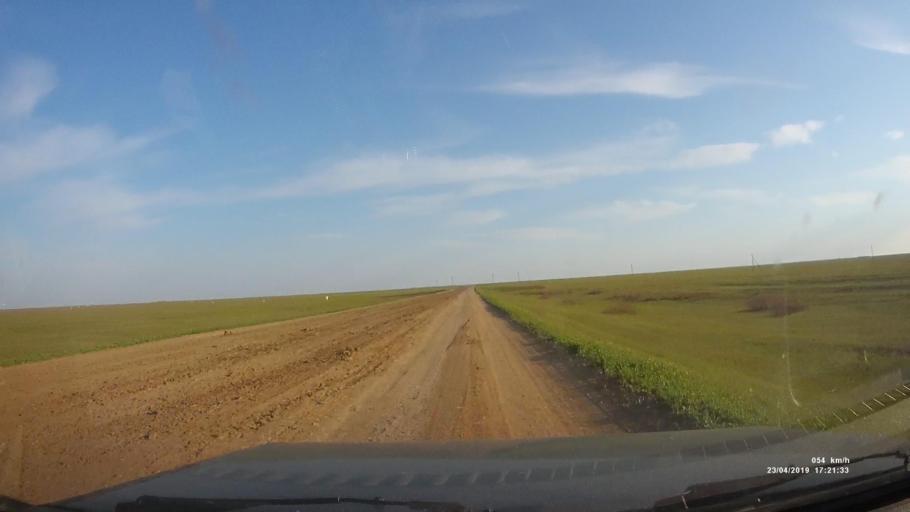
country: RU
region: Kalmykiya
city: Priyutnoye
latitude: 46.1752
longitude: 43.5055
